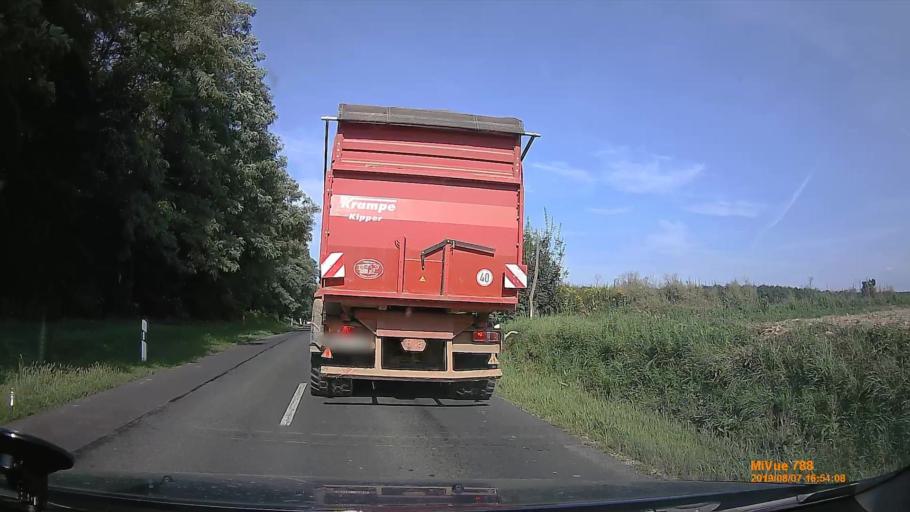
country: HU
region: Zala
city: Lenti
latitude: 46.6854
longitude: 16.7100
